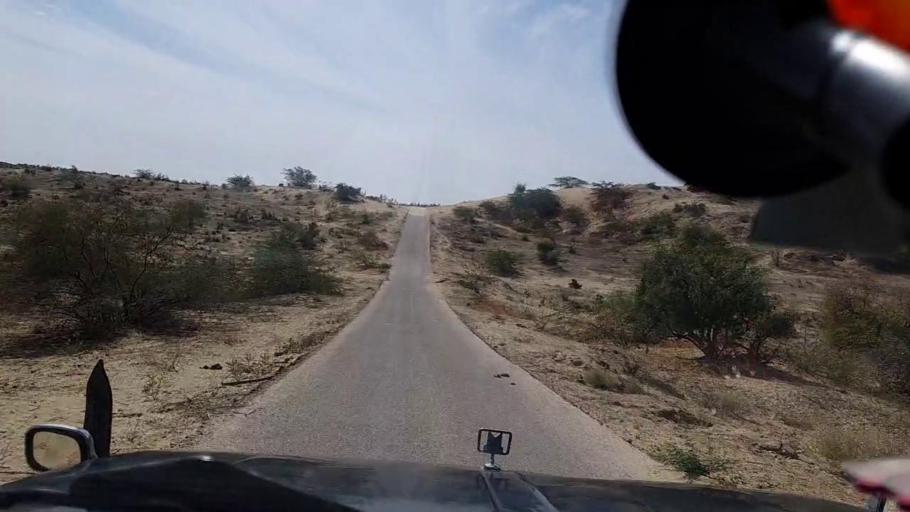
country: PK
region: Sindh
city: Diplo
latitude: 24.3997
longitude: 69.5887
